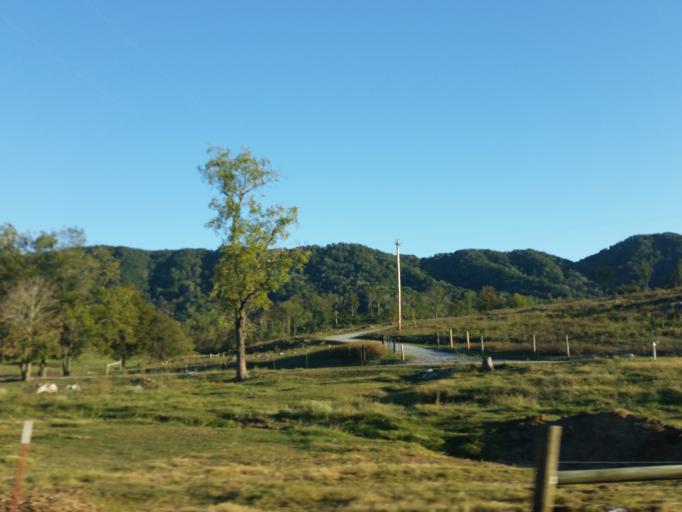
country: US
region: Tennessee
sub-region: Grainger County
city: Rutledge
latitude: 36.3500
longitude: -83.4488
